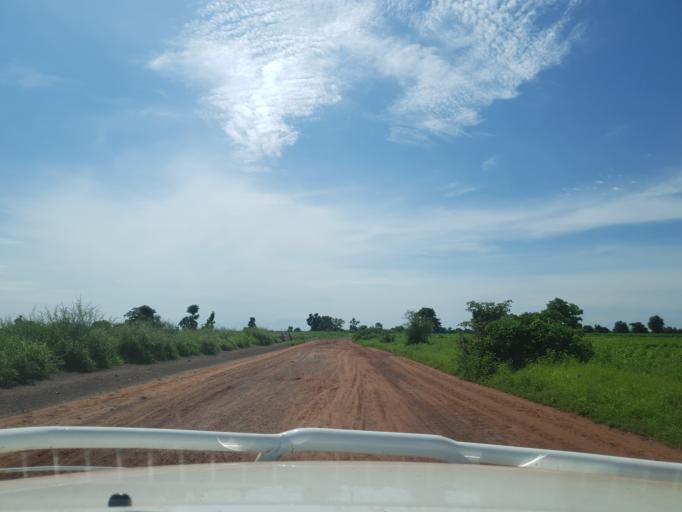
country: ML
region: Koulikoro
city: Banamba
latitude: 13.2801
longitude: -7.5520
